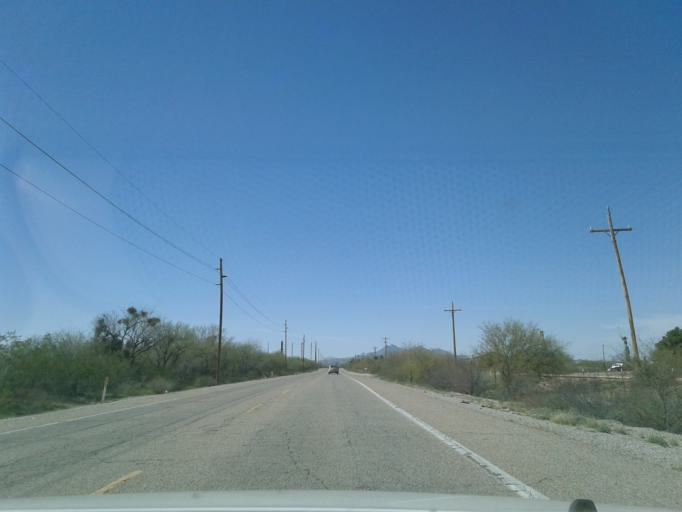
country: US
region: Arizona
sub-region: Pima County
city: Avra Valley
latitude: 32.3933
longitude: -111.2816
